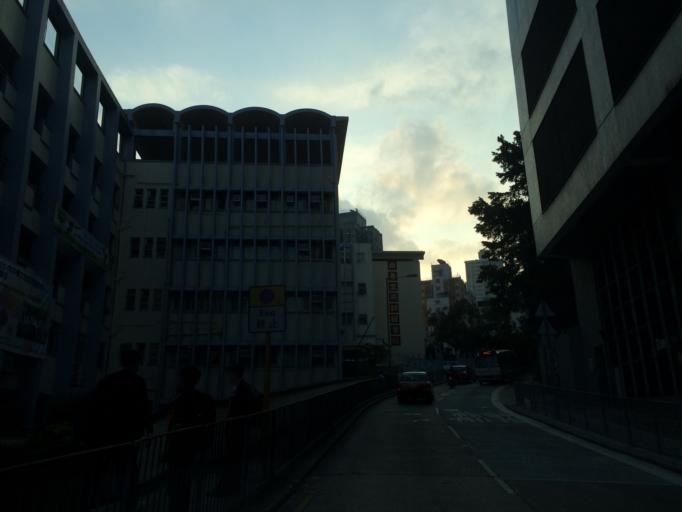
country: HK
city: Hong Kong
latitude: 22.2860
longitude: 114.1452
